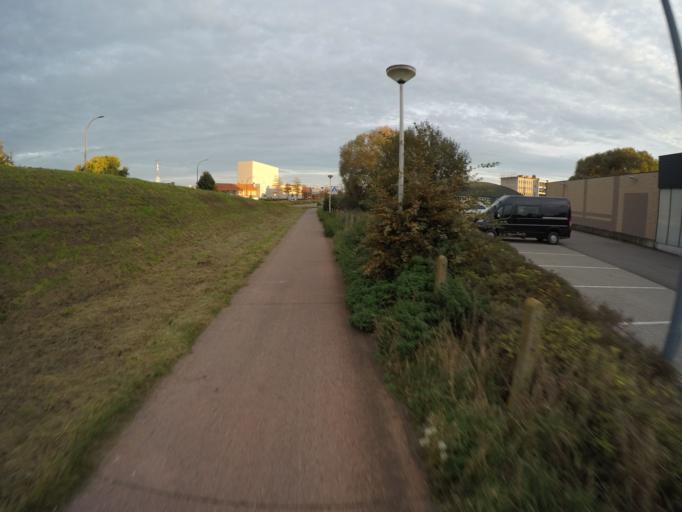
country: BE
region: Flanders
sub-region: Provincie Antwerpen
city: Zwijndrecht
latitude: 51.2141
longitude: 4.3398
